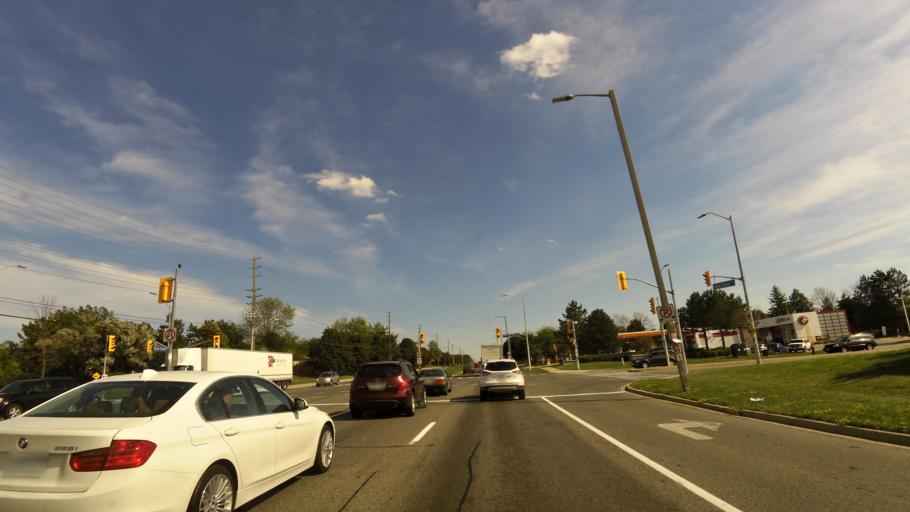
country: CA
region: Ontario
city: Mississauga
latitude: 43.5401
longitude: -79.7055
